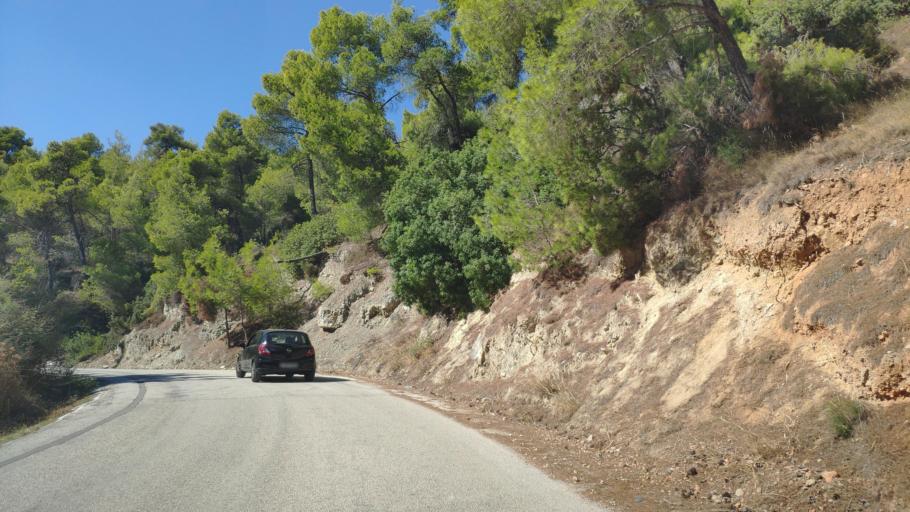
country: GR
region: Attica
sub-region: Nomarchia Anatolikis Attikis
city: Kouvaras
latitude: 37.8402
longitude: 23.9958
